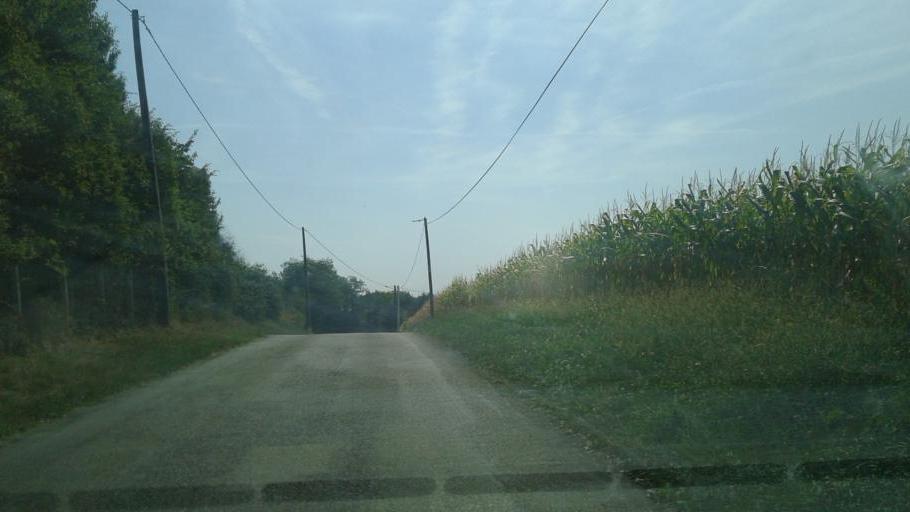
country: FR
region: Rhone-Alpes
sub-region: Departement de l'Ain
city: Tramoyes
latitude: 45.8697
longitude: 4.9747
